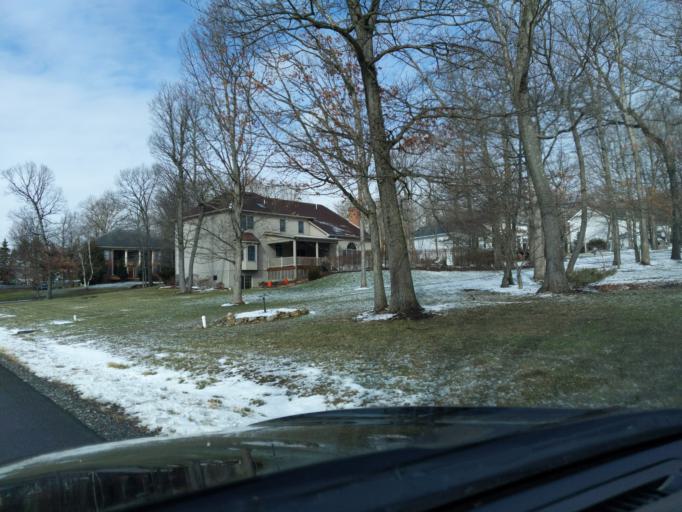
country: US
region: Pennsylvania
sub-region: Blair County
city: Lakemont
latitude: 40.4700
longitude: -78.3750
